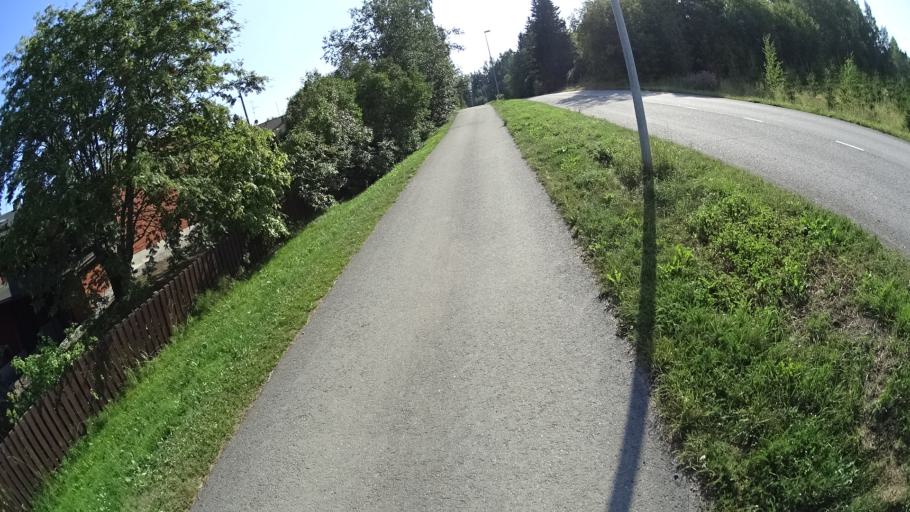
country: FI
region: Uusimaa
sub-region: Porvoo
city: Porvoo
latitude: 60.4128
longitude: 25.6527
